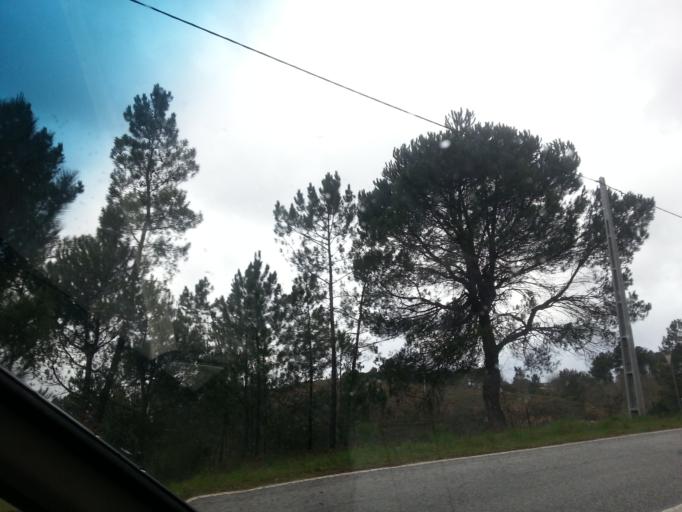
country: PT
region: Viseu
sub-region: Viseu
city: Rio de Loba
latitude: 40.6180
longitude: -7.8662
